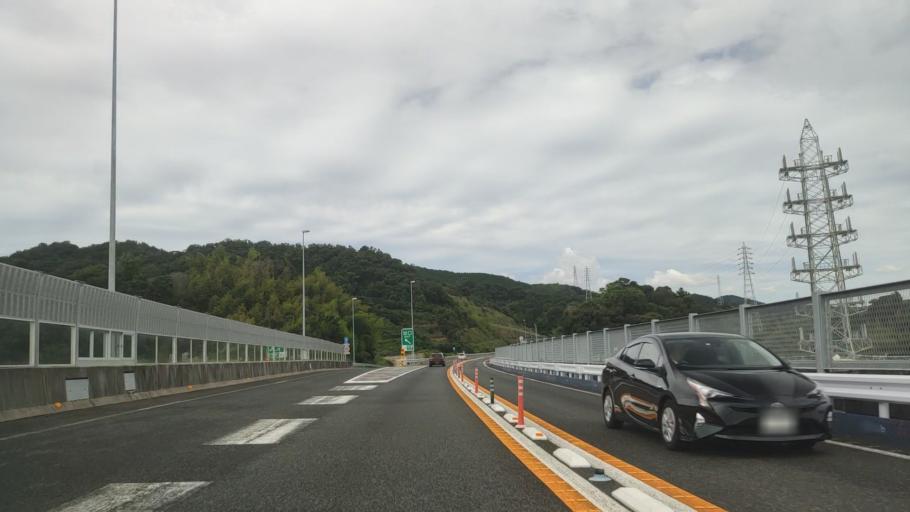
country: JP
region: Wakayama
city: Gobo
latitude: 33.8237
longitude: 135.2209
